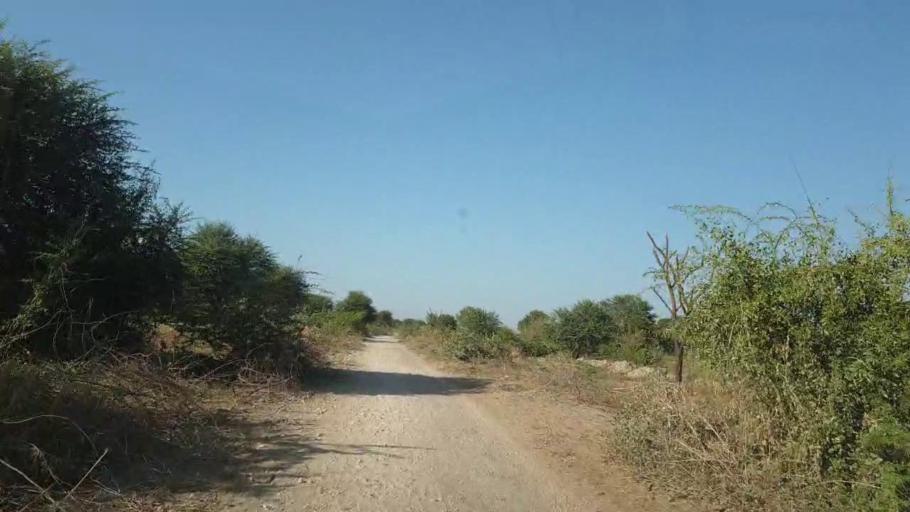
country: PK
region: Sindh
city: Kunri
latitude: 25.0590
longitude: 69.4420
